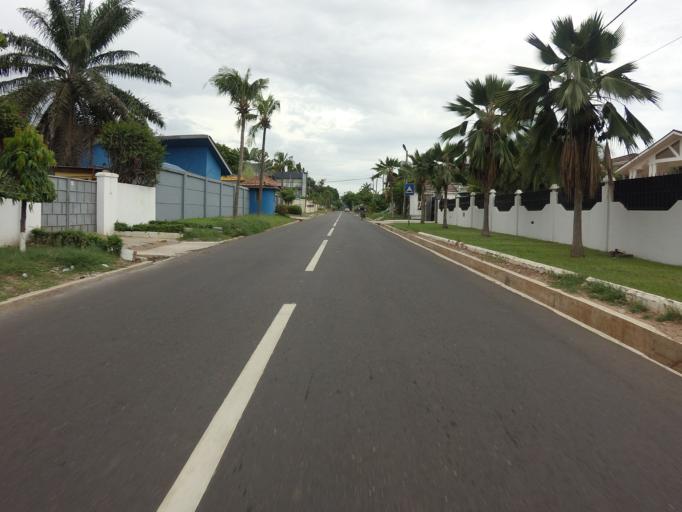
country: GH
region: Greater Accra
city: Dome
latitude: 5.6132
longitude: -0.2071
